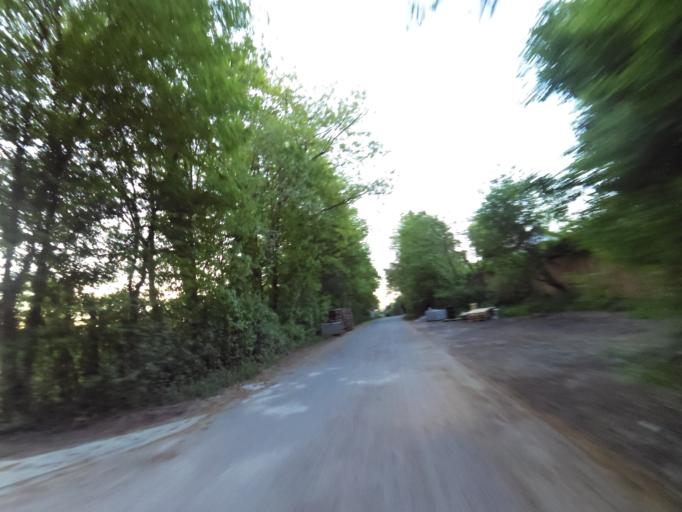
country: DE
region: North Rhine-Westphalia
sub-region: Regierungsbezirk Koln
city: Wachtberg
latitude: 50.6803
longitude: 7.0658
